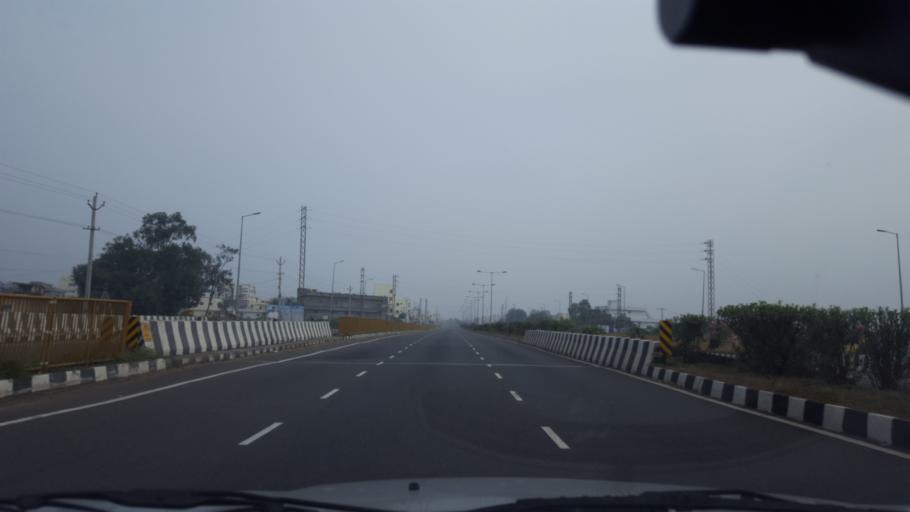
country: IN
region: Andhra Pradesh
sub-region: Prakasam
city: pedda nakkalapalem
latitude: 15.9761
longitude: 80.0984
